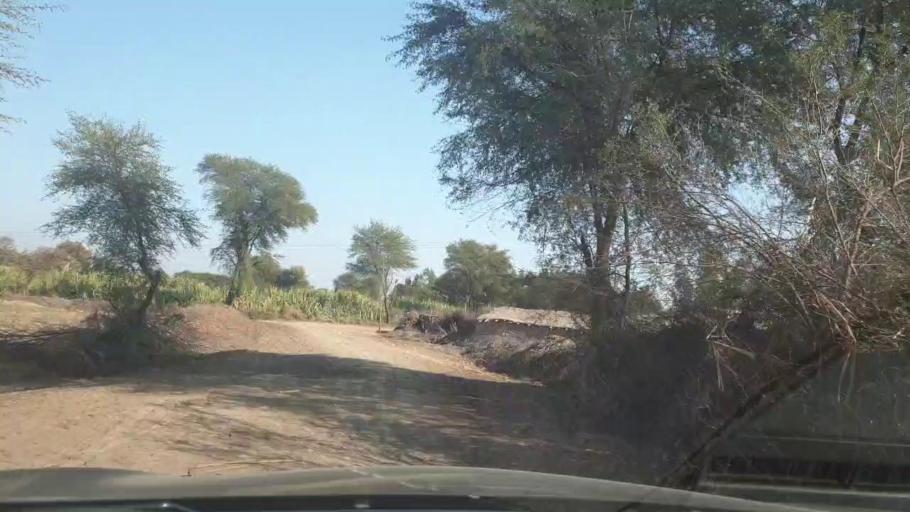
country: PK
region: Sindh
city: Khairpur
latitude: 28.1344
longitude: 69.6067
